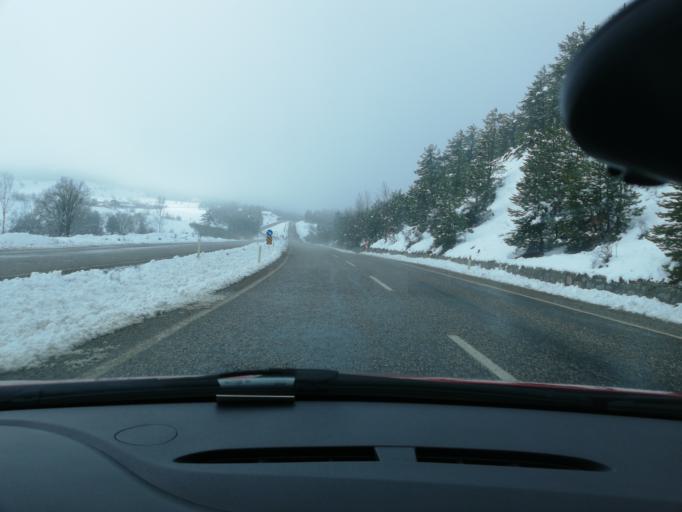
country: TR
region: Kastamonu
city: Akkaya
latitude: 41.2905
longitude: 33.4740
